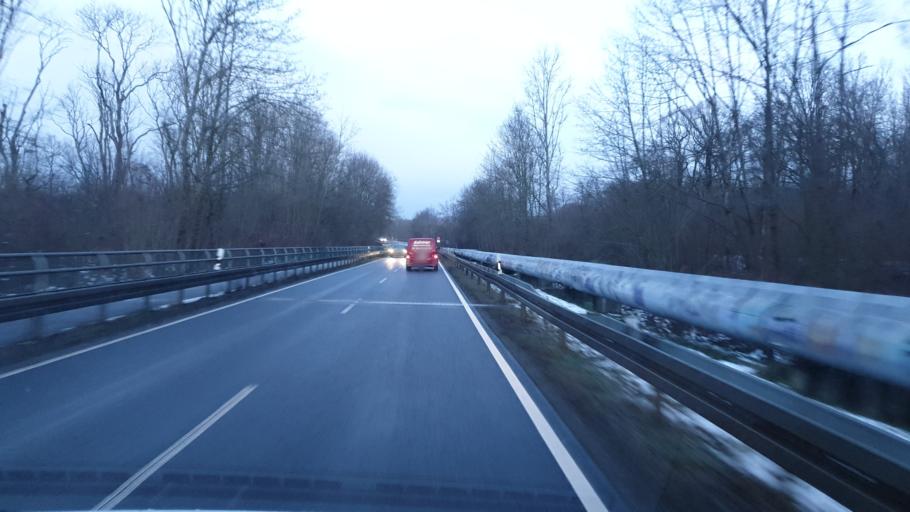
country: DE
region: Saxony
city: Markkleeberg
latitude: 51.2972
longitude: 12.3466
